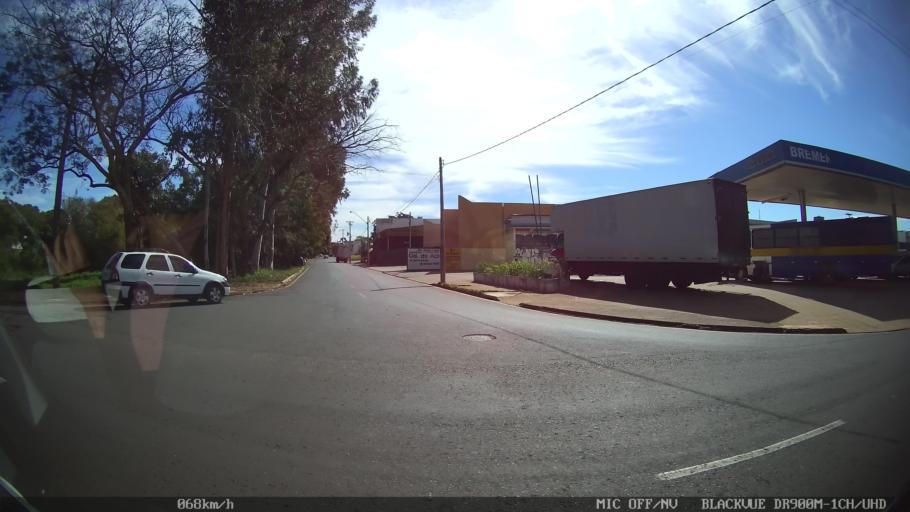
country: BR
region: Sao Paulo
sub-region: Sao Jose Do Rio Preto
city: Sao Jose do Rio Preto
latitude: -20.8439
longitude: -49.3580
